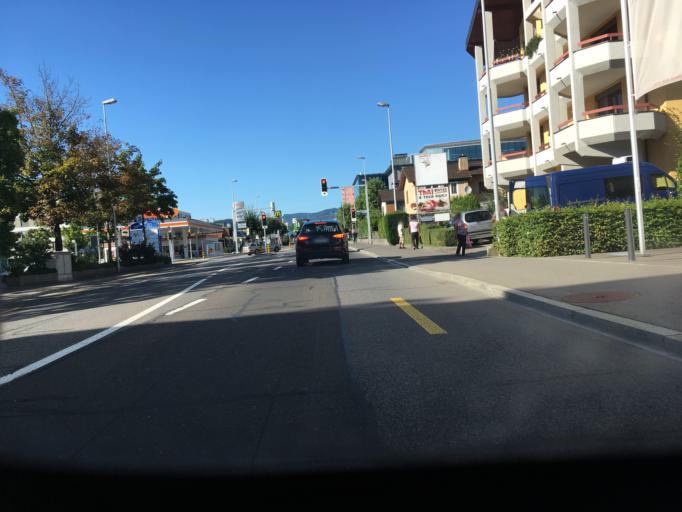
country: CH
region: Zug
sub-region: Zug
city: Zug
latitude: 47.1840
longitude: 8.5202
